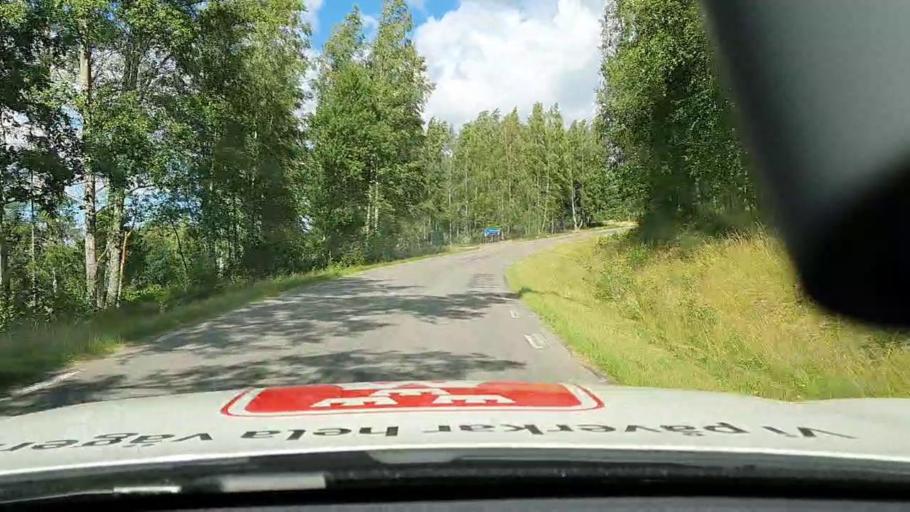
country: SE
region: Vaestra Goetaland
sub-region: Karlsborgs Kommun
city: Molltorp
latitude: 58.5979
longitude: 14.2641
